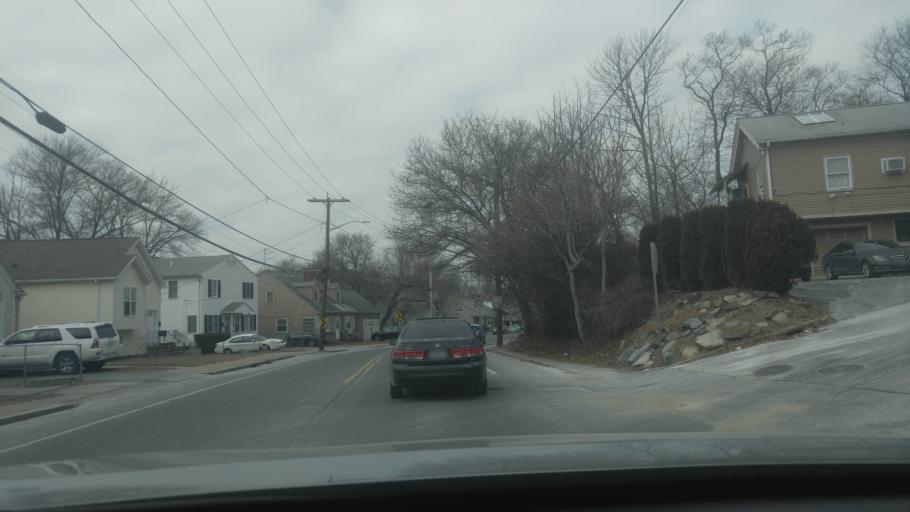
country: US
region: Rhode Island
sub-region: Providence County
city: North Providence
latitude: 41.8293
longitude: -71.4627
